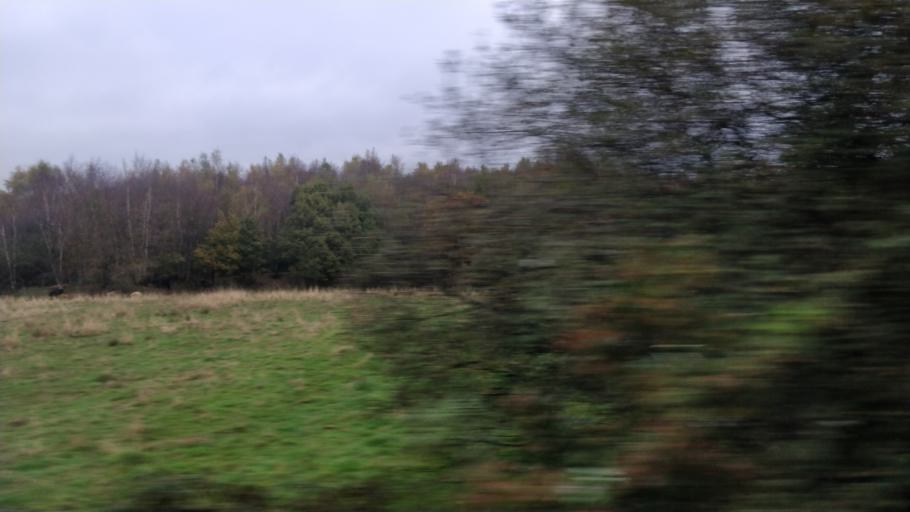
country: GB
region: England
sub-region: Borough of Wigan
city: Shevington
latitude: 53.5569
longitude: -2.6744
